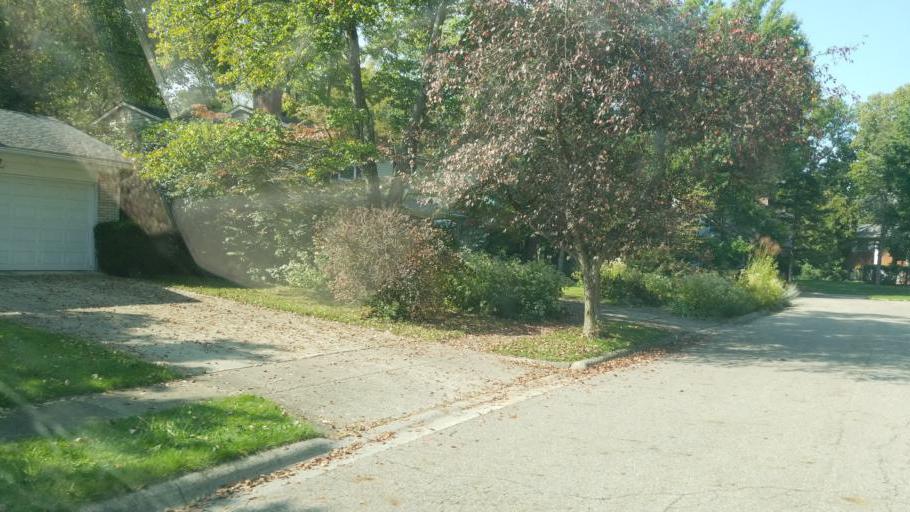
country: US
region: Ohio
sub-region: Franklin County
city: Worthington
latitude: 40.0776
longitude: -83.0243
